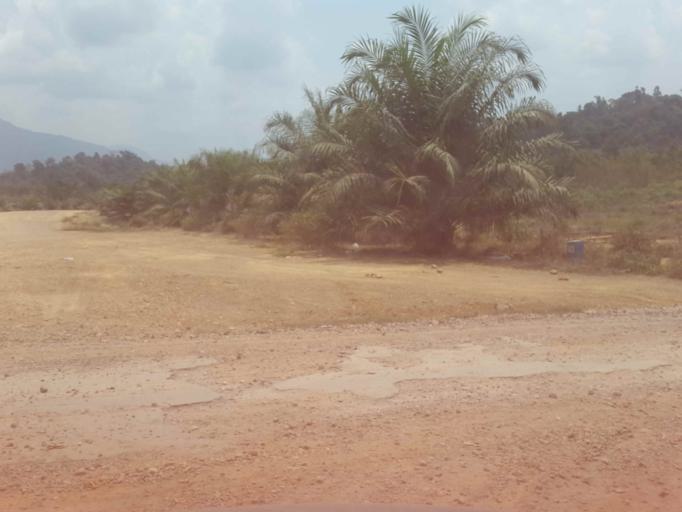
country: MY
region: Sarawak
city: Simanggang
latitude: 1.0049
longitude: 111.8846
